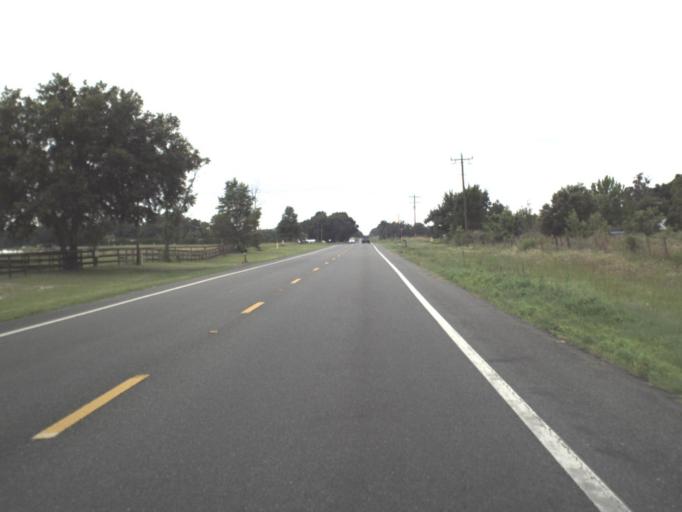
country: US
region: Florida
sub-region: Levy County
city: Williston
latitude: 29.3154
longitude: -82.4517
